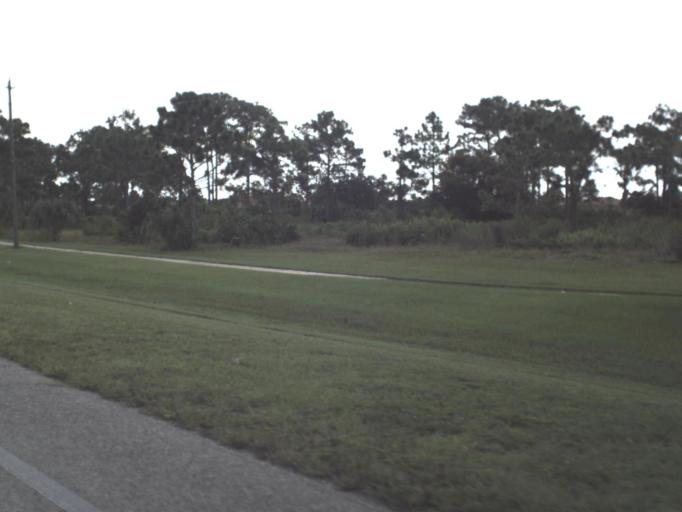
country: US
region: Florida
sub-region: Sarasota County
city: Plantation
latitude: 27.0496
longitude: -82.3721
